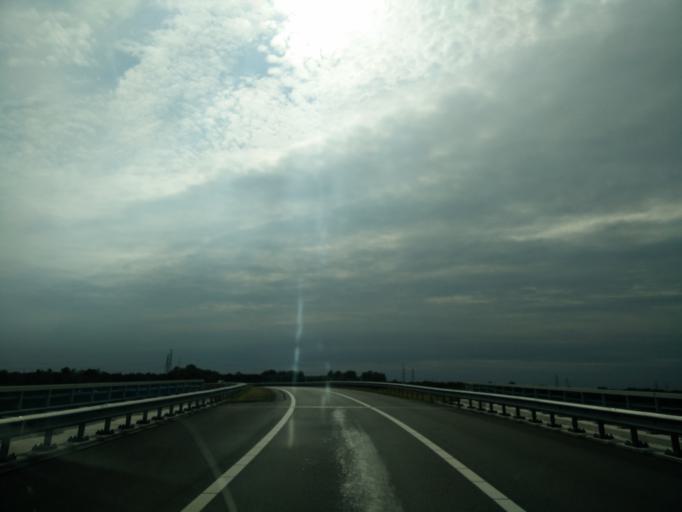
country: NL
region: Drenthe
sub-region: Gemeente Assen
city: Assen
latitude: 52.9707
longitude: 6.5512
